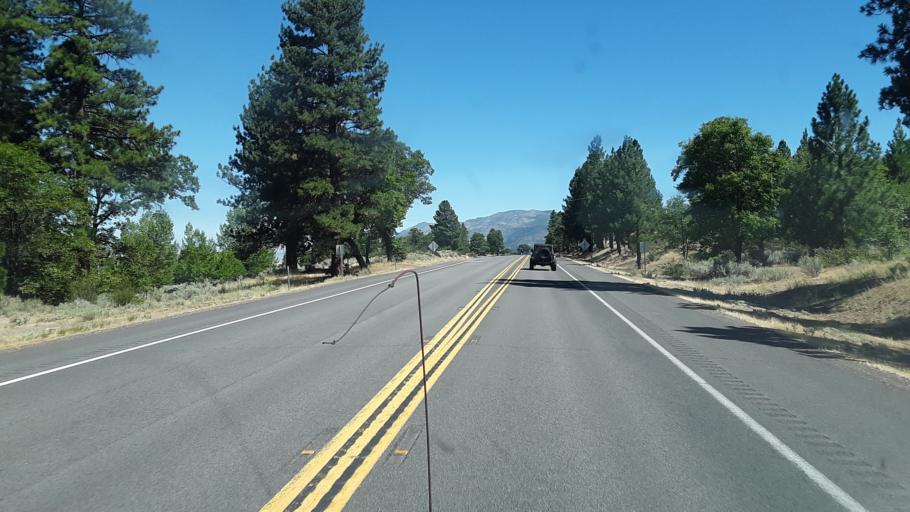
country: US
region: California
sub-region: Lassen County
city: Janesville
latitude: 40.2207
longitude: -120.4321
